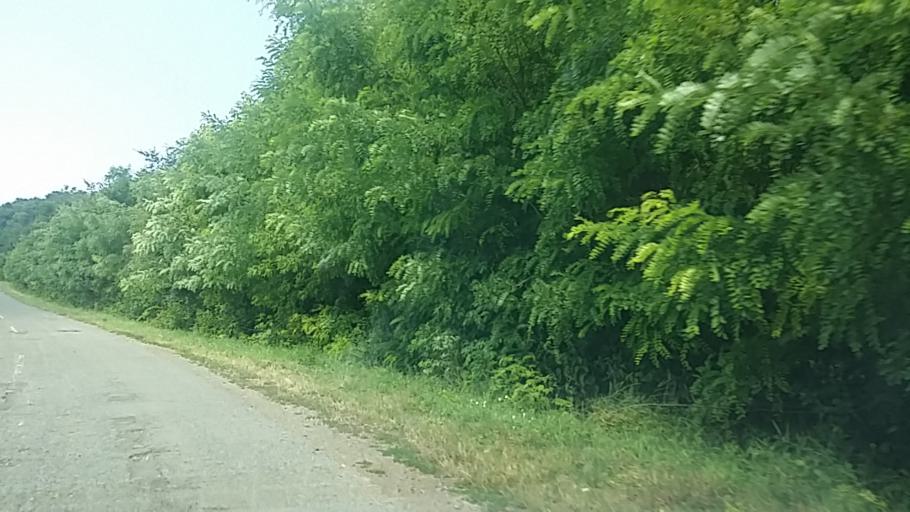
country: HU
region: Nograd
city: Matraverebely
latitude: 47.9680
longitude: 19.7616
